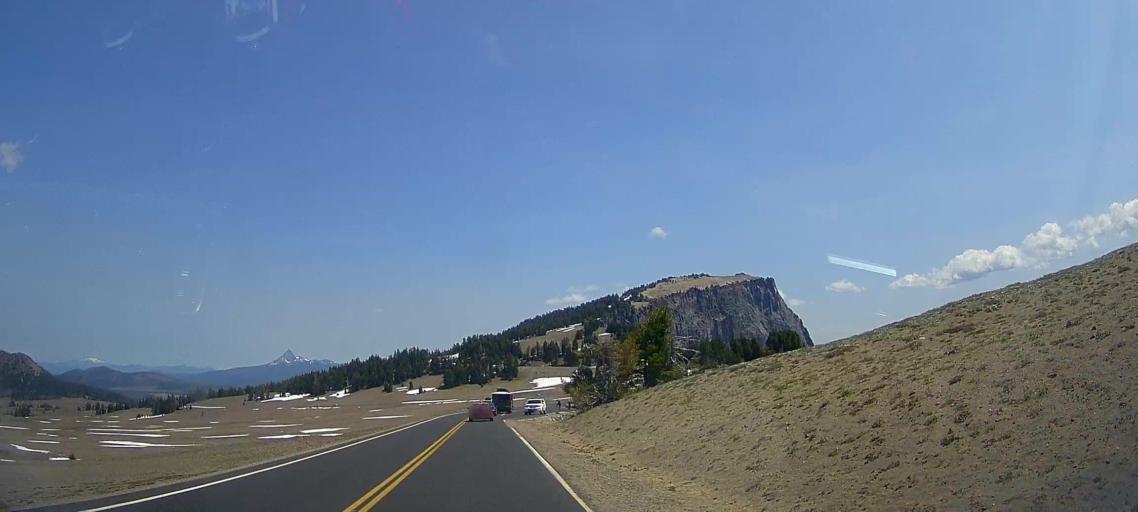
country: US
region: Oregon
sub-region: Jackson County
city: Shady Cove
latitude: 42.9617
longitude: -122.1560
